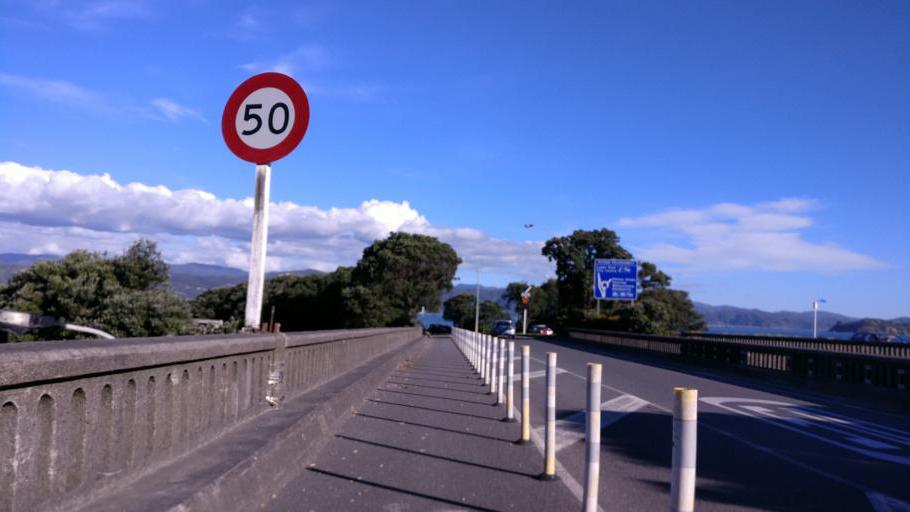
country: NZ
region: Wellington
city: Petone
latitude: -41.2230
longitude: 174.8598
